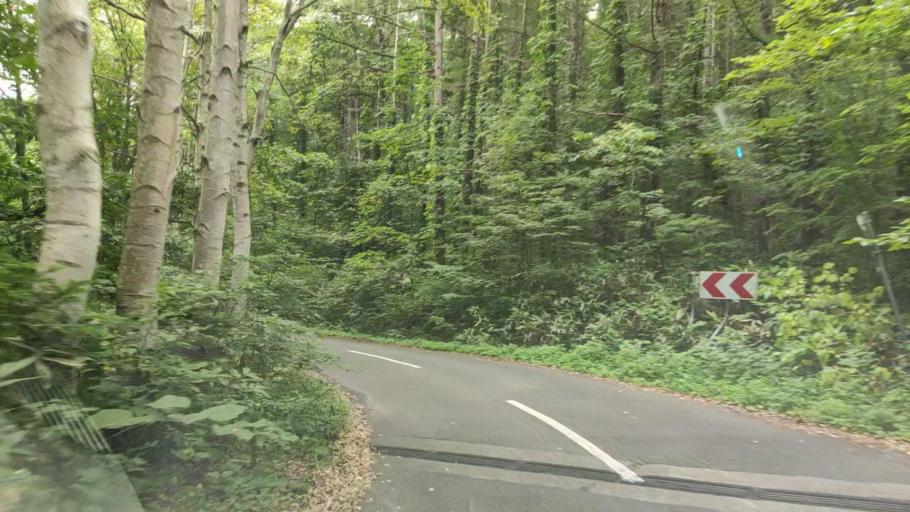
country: JP
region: Hokkaido
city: Otaru
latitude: 43.1954
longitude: 140.9809
